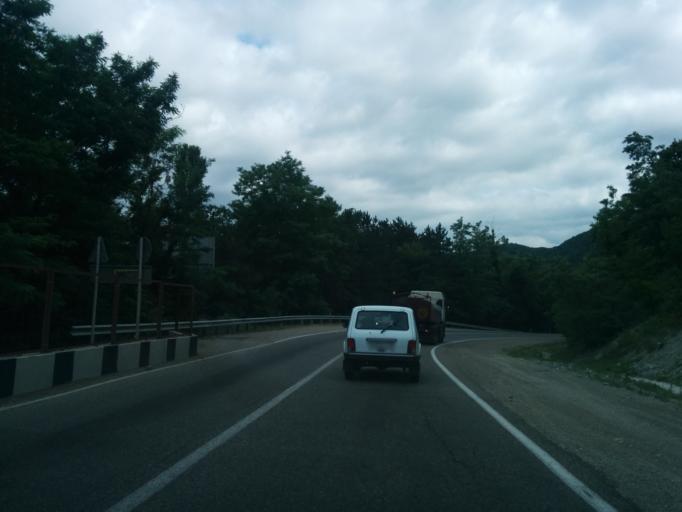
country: RU
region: Krasnodarskiy
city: Agoy
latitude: 44.1370
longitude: 39.0530
